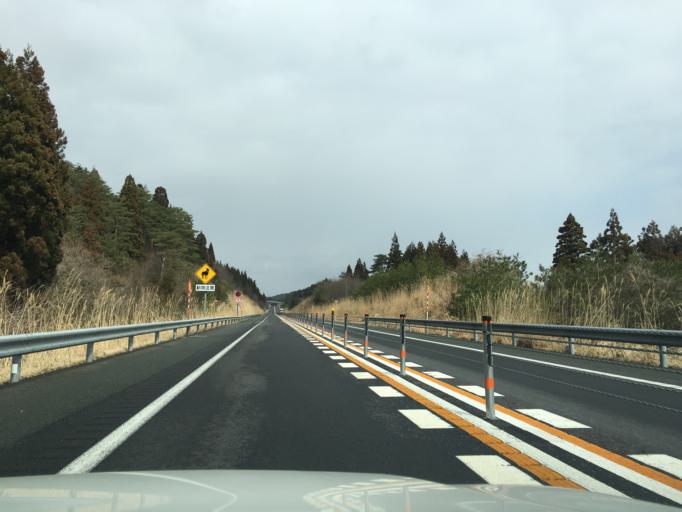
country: JP
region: Akita
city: Tenno
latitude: 39.9831
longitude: 140.0949
